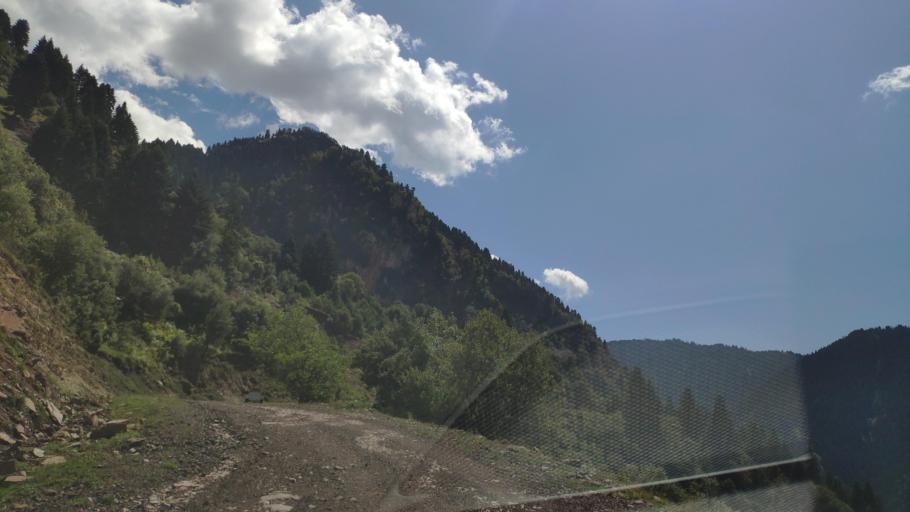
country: GR
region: Central Greece
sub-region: Nomos Evrytanias
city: Kerasochori
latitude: 39.1364
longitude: 21.6573
